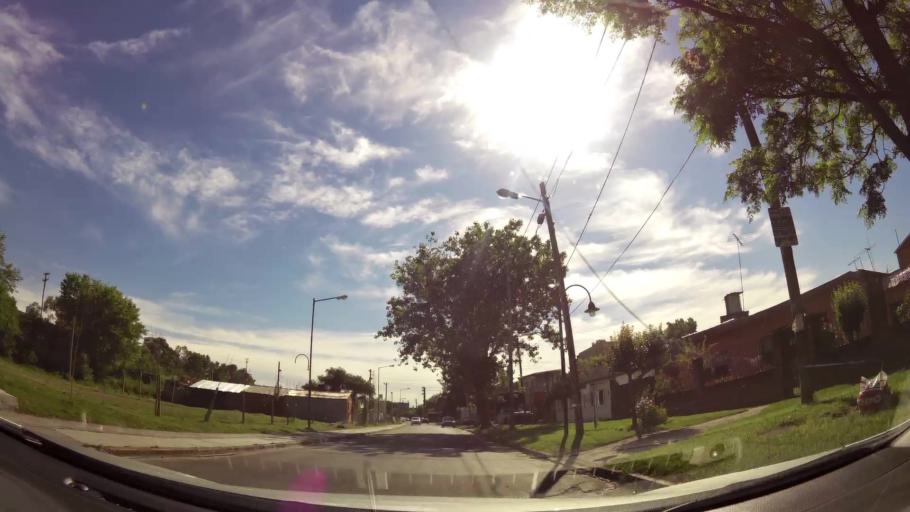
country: AR
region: Buenos Aires
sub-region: Partido de Tigre
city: Tigre
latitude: -34.4750
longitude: -58.5799
